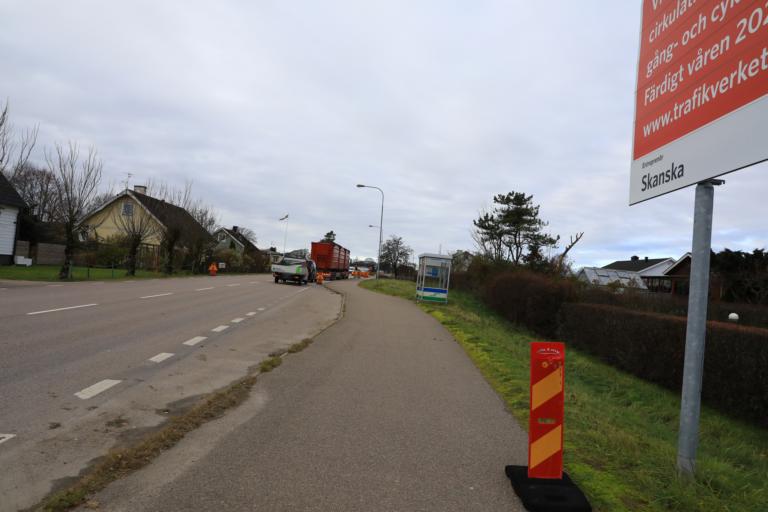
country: SE
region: Halland
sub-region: Varbergs Kommun
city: Tvaaker
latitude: 57.0449
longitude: 12.3872
